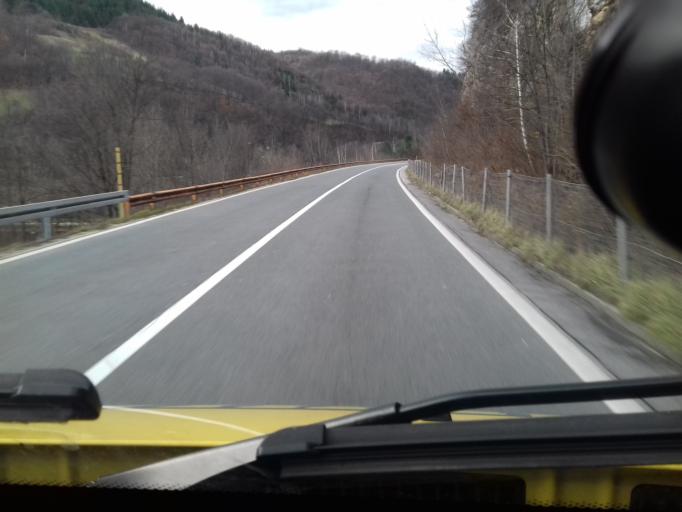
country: BA
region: Federation of Bosnia and Herzegovina
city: Kacuni
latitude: 44.1298
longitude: 17.9437
